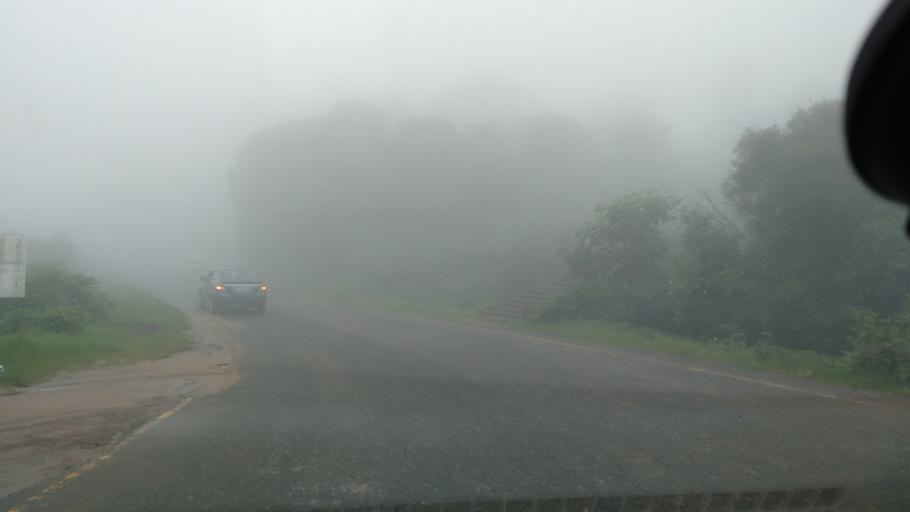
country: IN
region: Meghalaya
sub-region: East Khasi Hills
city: Cherrapunji
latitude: 25.2876
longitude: 91.7165
